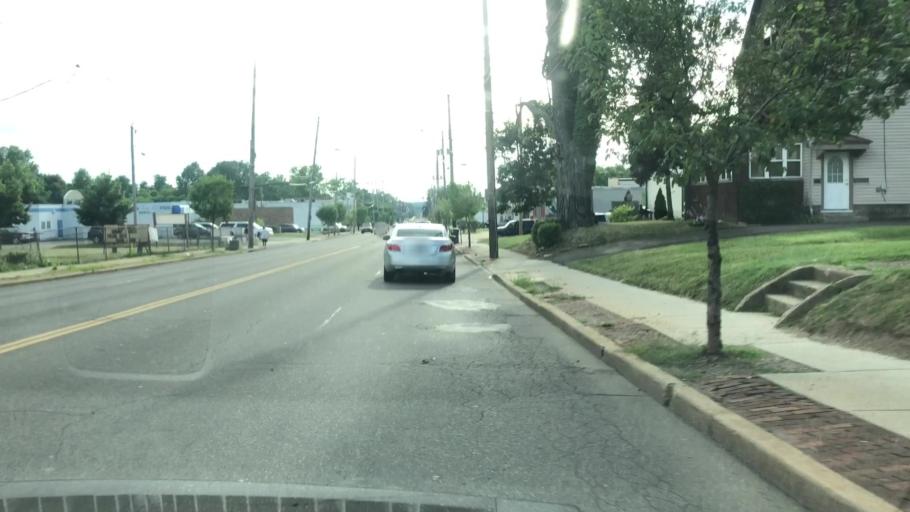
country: US
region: Ohio
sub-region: Summit County
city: Akron
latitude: 41.0844
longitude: -81.5498
